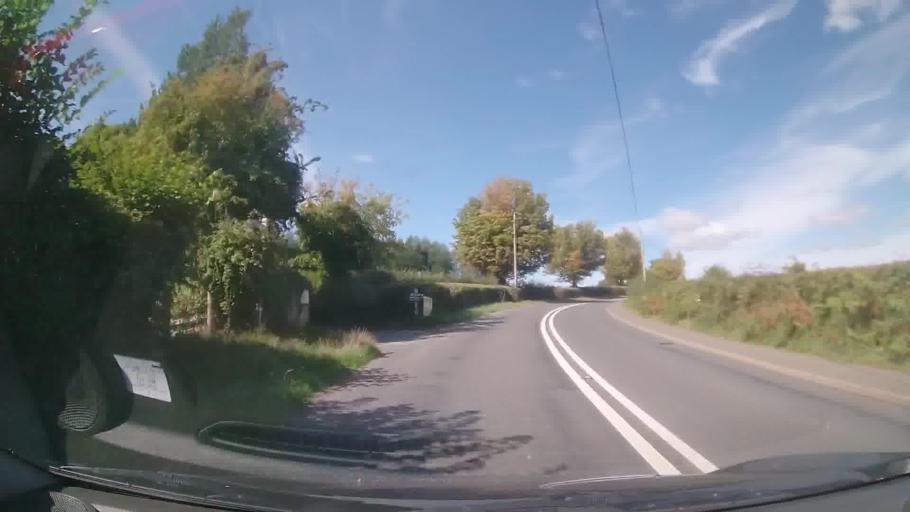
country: GB
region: Wales
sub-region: Sir Powys
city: Hay
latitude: 52.0783
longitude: -3.1319
